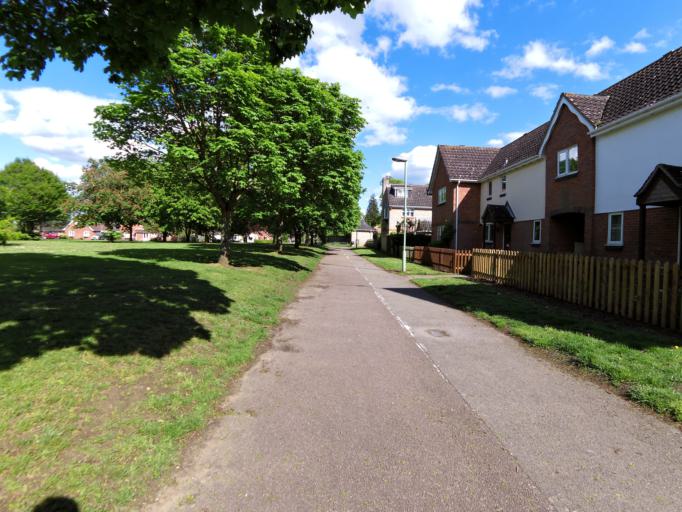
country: GB
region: England
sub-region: Suffolk
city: Thurston
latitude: 52.2508
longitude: 0.8136
